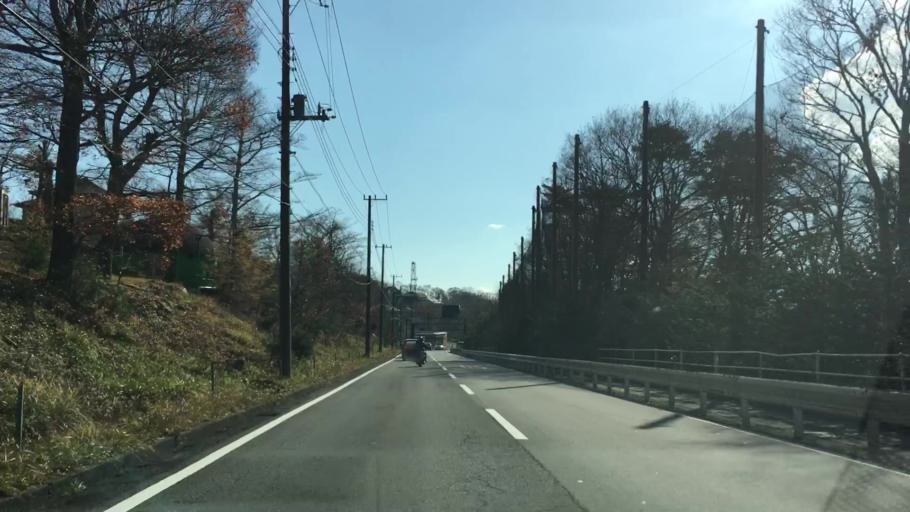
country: JP
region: Shizuoka
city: Gotemba
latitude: 35.3726
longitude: 138.8602
